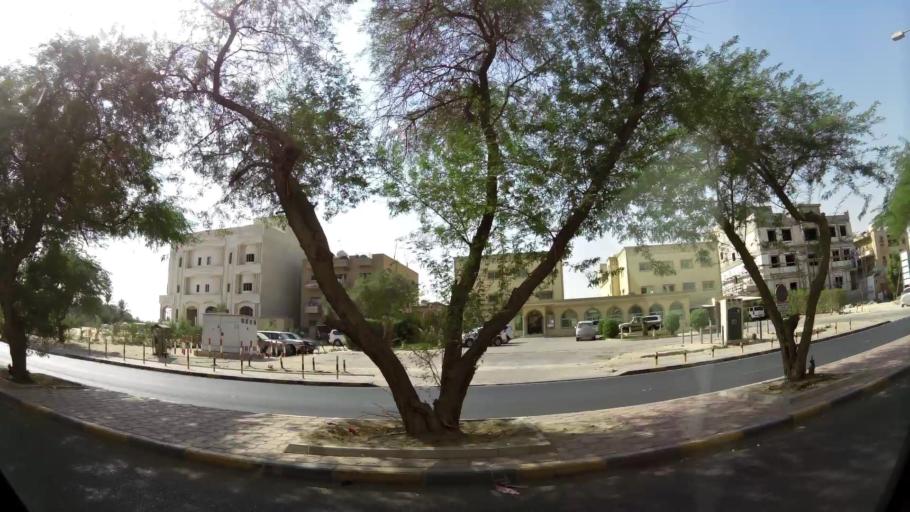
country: KW
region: Al Ahmadi
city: Al Fahahil
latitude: 29.0814
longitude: 48.1231
